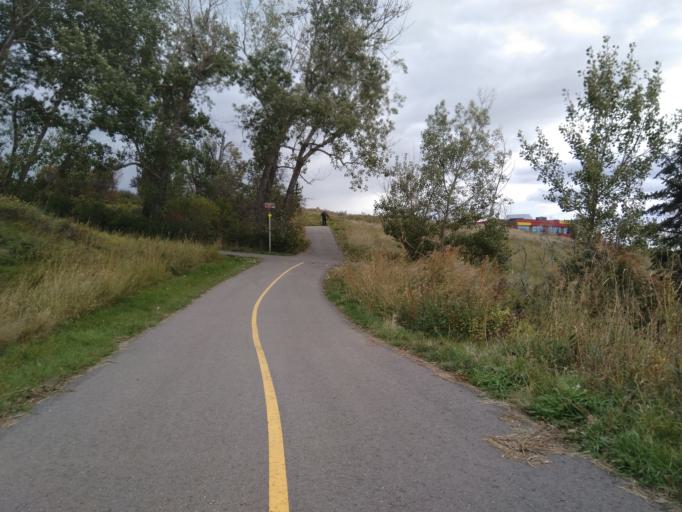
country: CA
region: Alberta
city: Calgary
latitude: 51.0436
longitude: -114.0070
